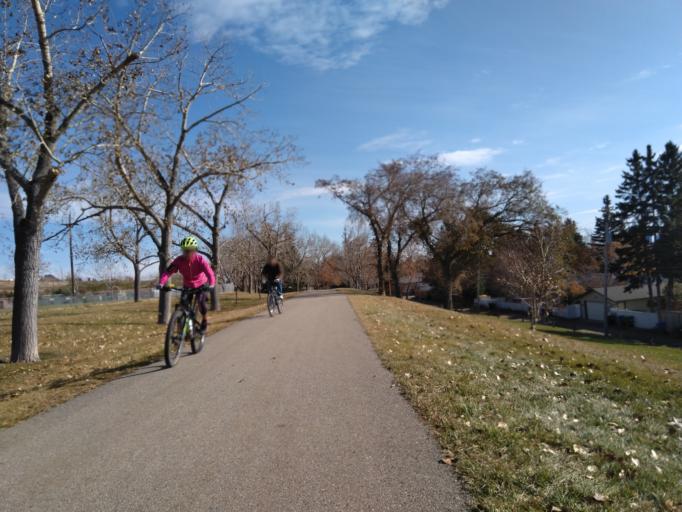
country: CA
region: Alberta
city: Calgary
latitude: 51.0923
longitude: -114.1095
